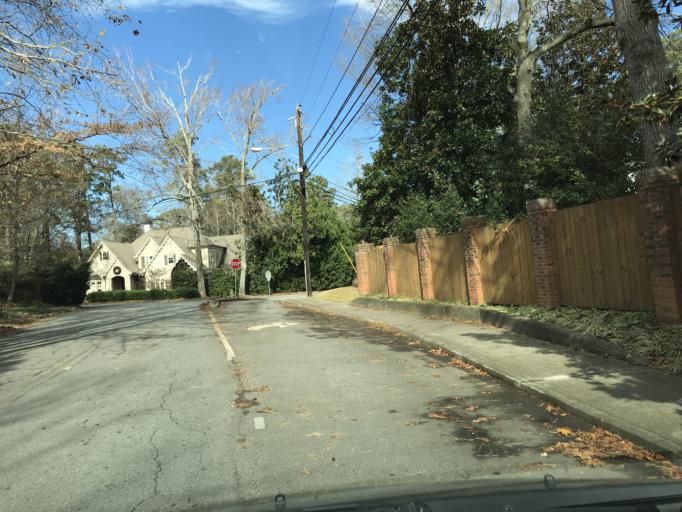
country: US
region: Georgia
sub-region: DeKalb County
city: North Atlanta
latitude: 33.8771
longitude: -84.3475
